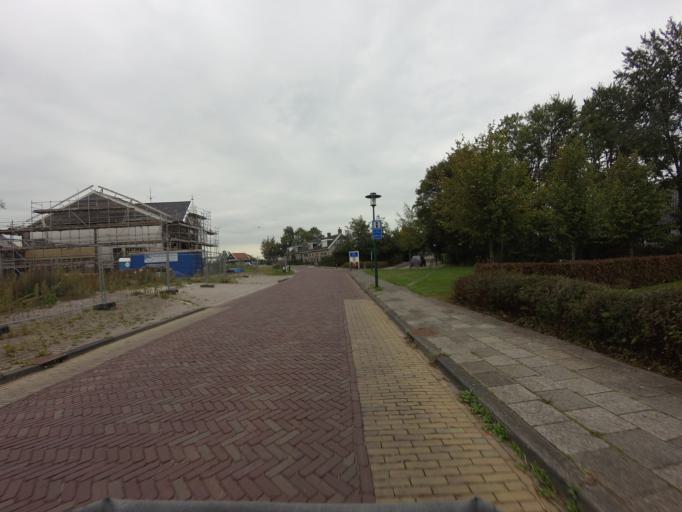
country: NL
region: Friesland
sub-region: Sudwest Fryslan
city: IJlst
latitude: 53.0093
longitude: 5.6076
